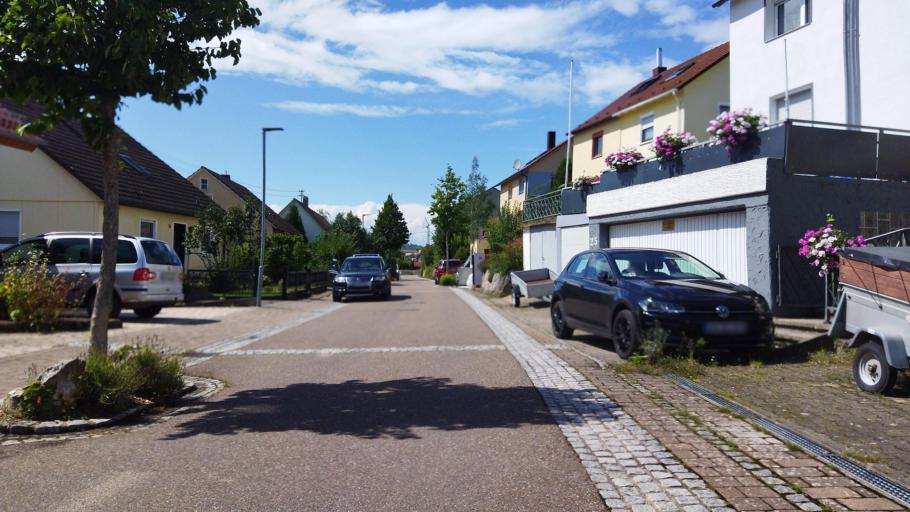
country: DE
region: Baden-Wuerttemberg
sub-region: Regierungsbezirk Stuttgart
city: Erligheim
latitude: 49.0174
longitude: 9.1047
